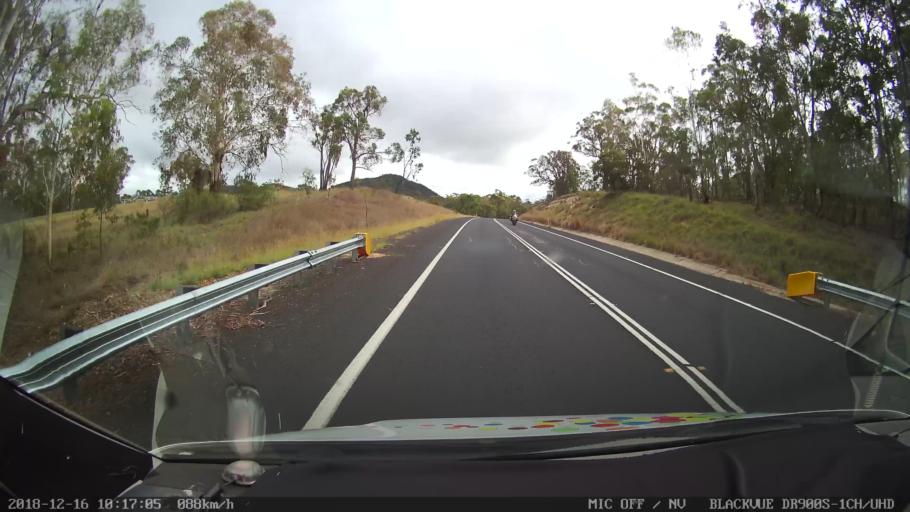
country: AU
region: New South Wales
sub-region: Tenterfield Municipality
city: Carrolls Creek
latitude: -29.2600
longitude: 151.9887
